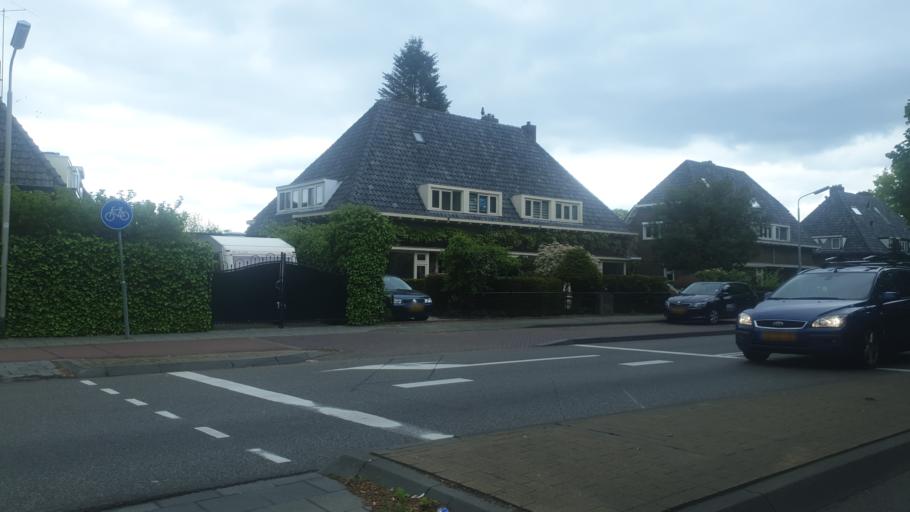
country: NL
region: Gelderland
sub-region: Gemeente Nijmegen
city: Nijmegen
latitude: 51.8085
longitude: 5.8457
